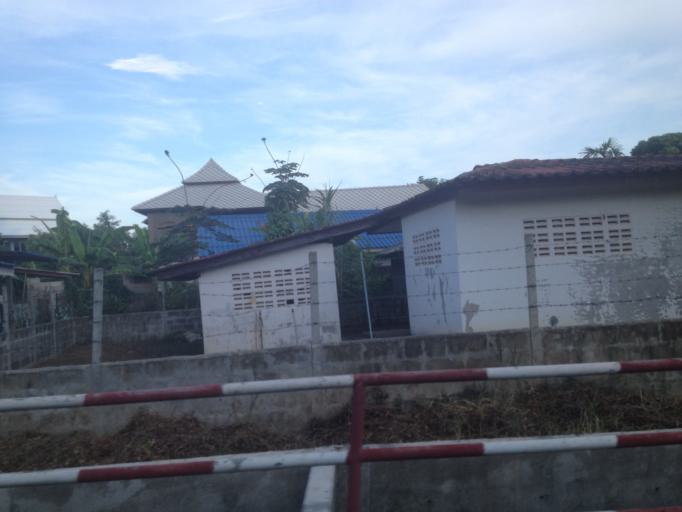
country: TH
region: Chiang Mai
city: Hang Dong
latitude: 18.7006
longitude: 98.9127
